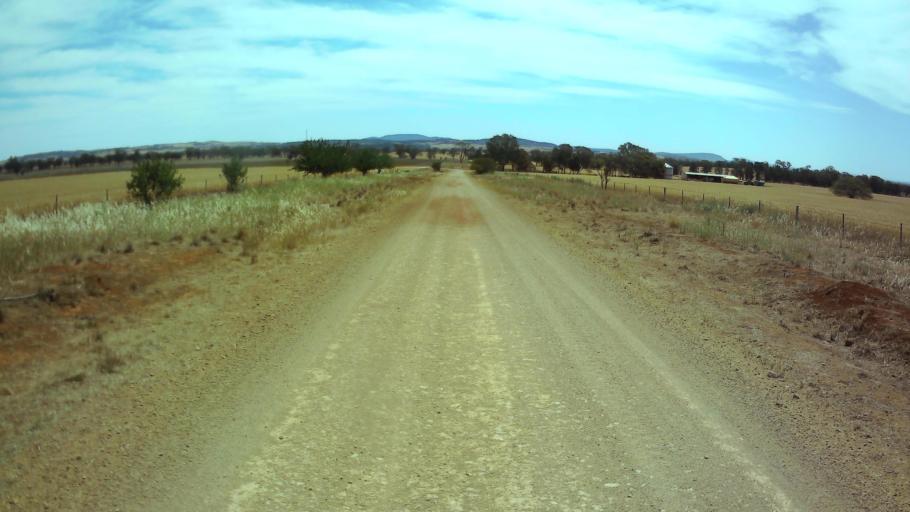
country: AU
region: New South Wales
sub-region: Weddin
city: Grenfell
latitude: -33.7496
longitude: 148.1502
